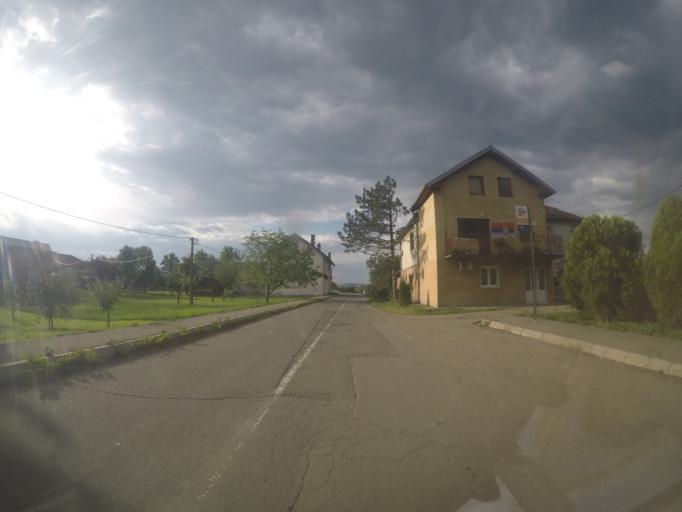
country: RS
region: Central Serbia
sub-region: Belgrade
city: Zemun
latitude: 44.9092
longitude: 20.4305
